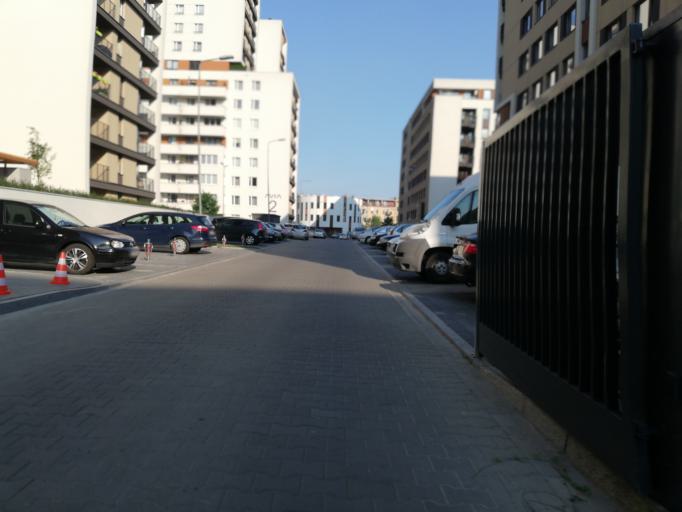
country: PL
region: Lesser Poland Voivodeship
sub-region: Krakow
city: Krakow
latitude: 50.0807
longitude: 20.0036
